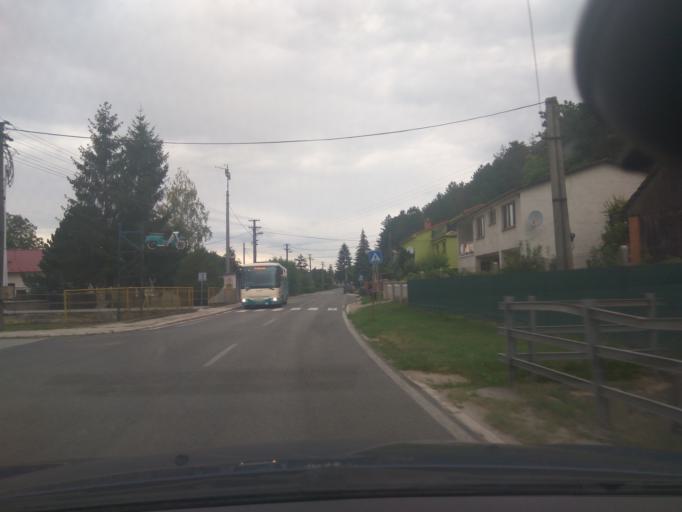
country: SK
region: Trnavsky
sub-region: Okres Trnava
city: Piestany
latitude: 48.6286
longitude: 17.8679
